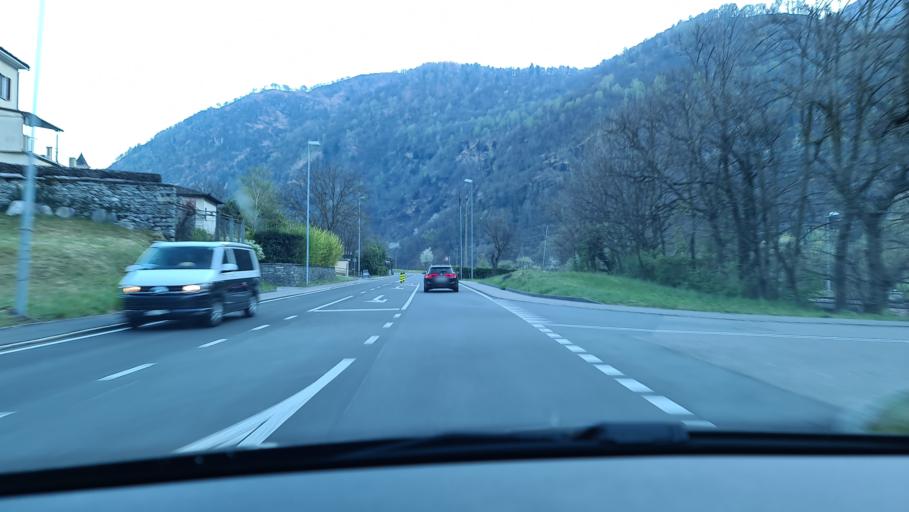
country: CH
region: Ticino
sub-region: Locarno District
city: Verscio
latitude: 46.2087
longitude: 8.7435
